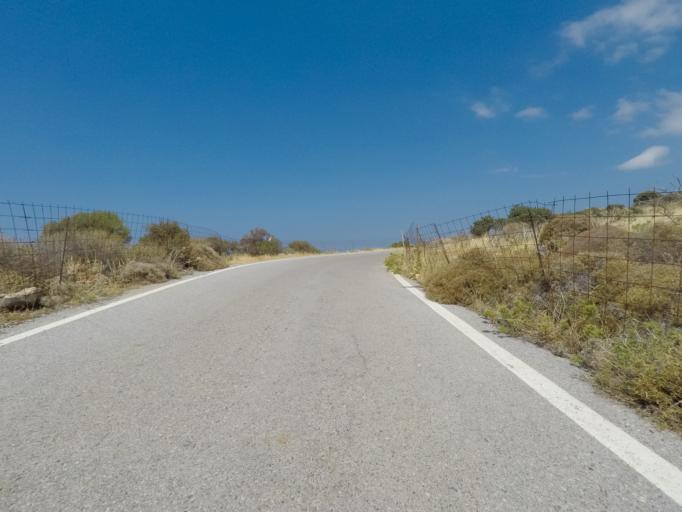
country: GR
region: Crete
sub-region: Nomos Lasithiou
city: Elounda
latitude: 35.3184
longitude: 25.6734
